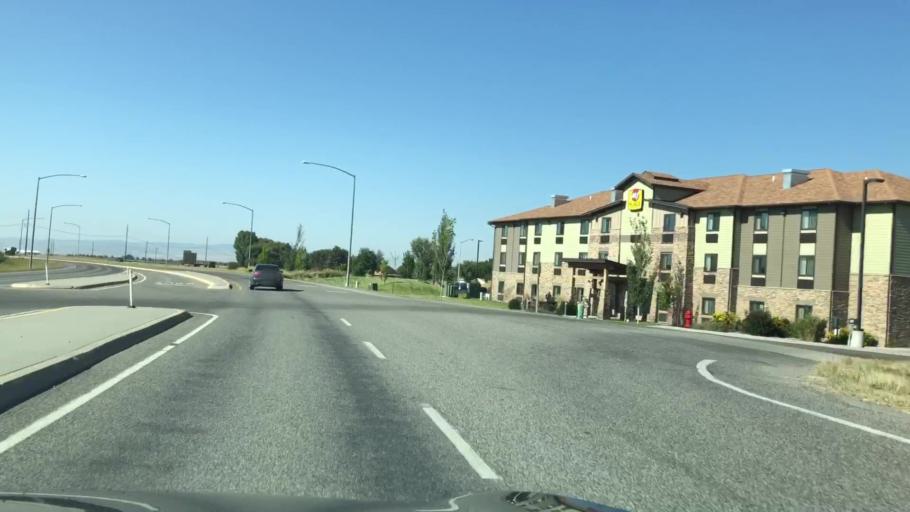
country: US
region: Montana
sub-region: Gallatin County
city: Bozeman
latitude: 45.7169
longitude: -111.0690
